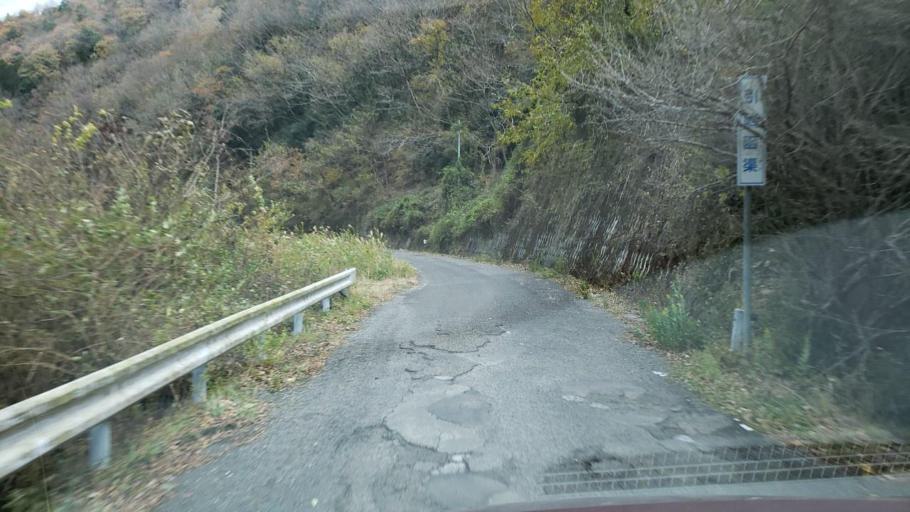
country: JP
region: Tokushima
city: Wakimachi
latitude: 34.1379
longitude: 134.2299
